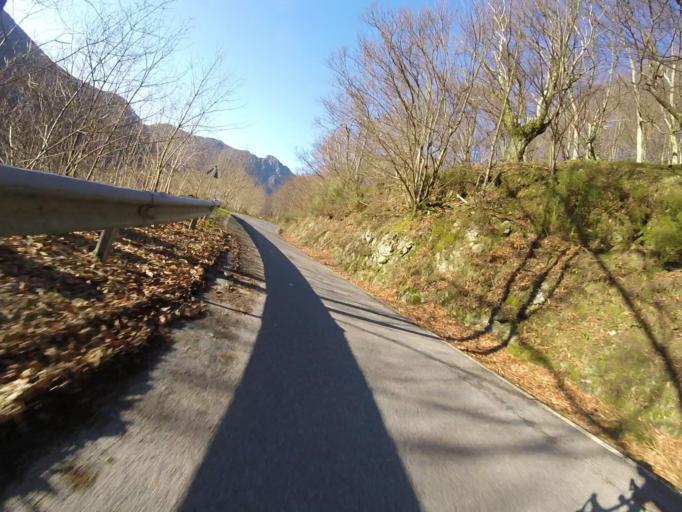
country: ES
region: Navarre
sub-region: Provincia de Navarra
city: Lesaka
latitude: 43.2616
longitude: -1.7639
